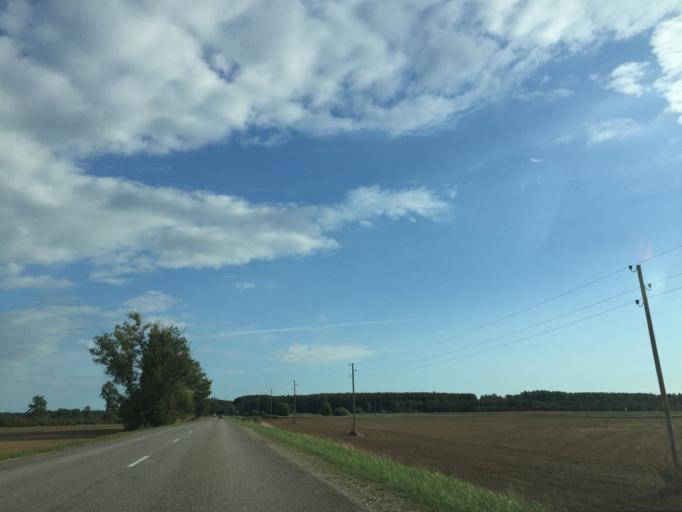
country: LV
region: Limbazu Rajons
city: Limbazi
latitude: 57.5097
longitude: 24.5102
